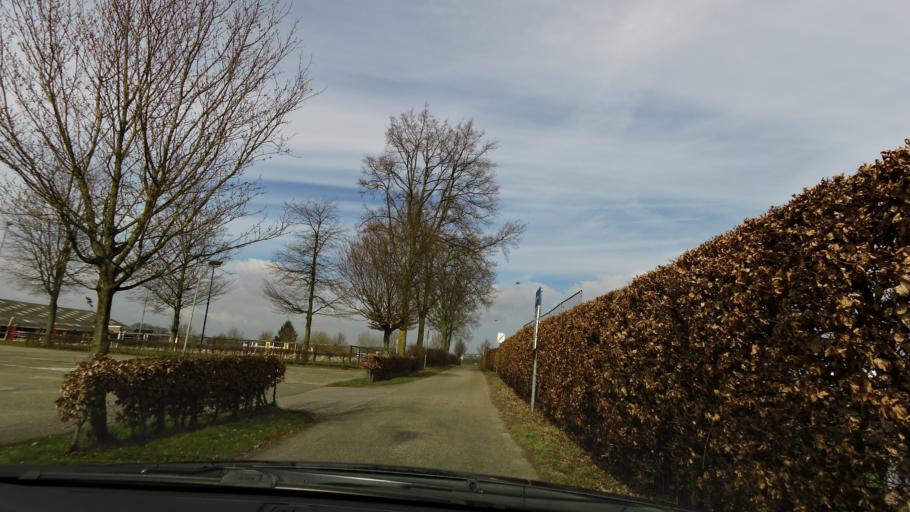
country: NL
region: Limburg
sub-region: Gemeente Simpelveld
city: Simpelveld
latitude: 50.8191
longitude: 5.9904
